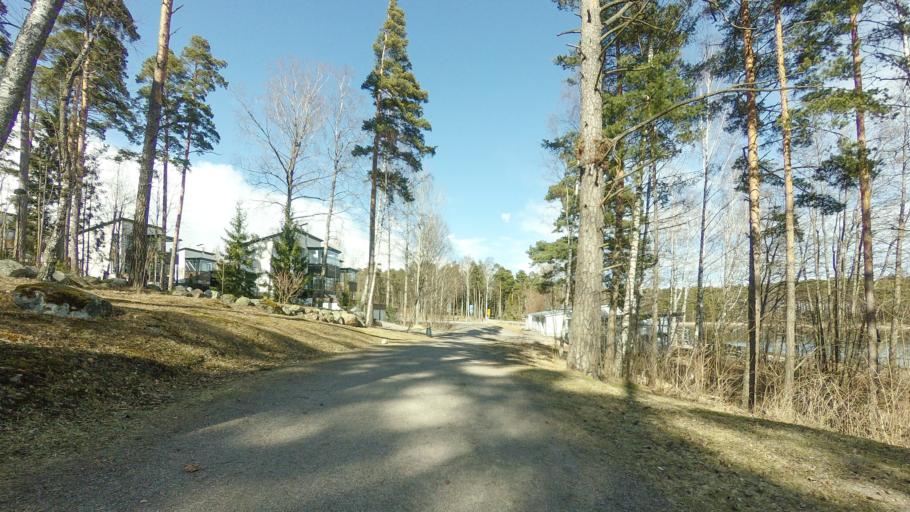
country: FI
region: Uusimaa
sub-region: Helsinki
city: Vantaa
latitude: 60.1973
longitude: 25.1273
